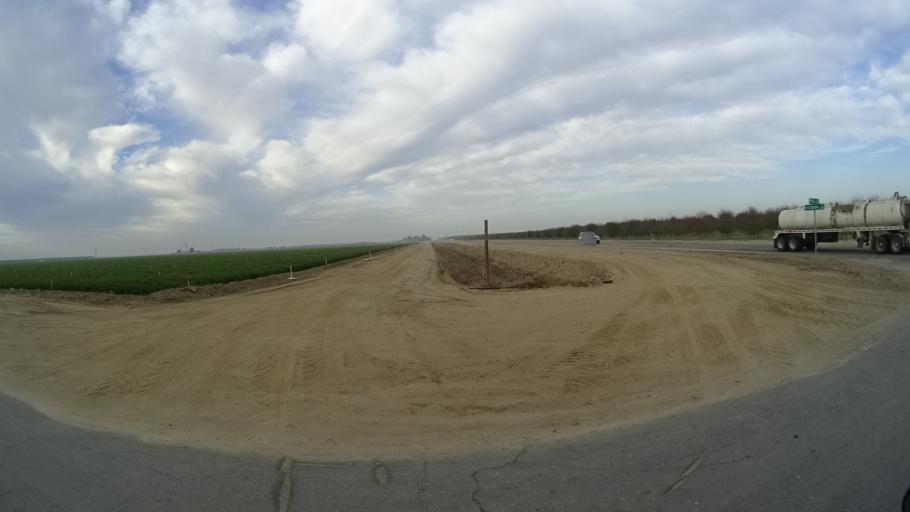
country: US
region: California
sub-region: Kern County
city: Rosedale
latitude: 35.4195
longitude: -119.1899
